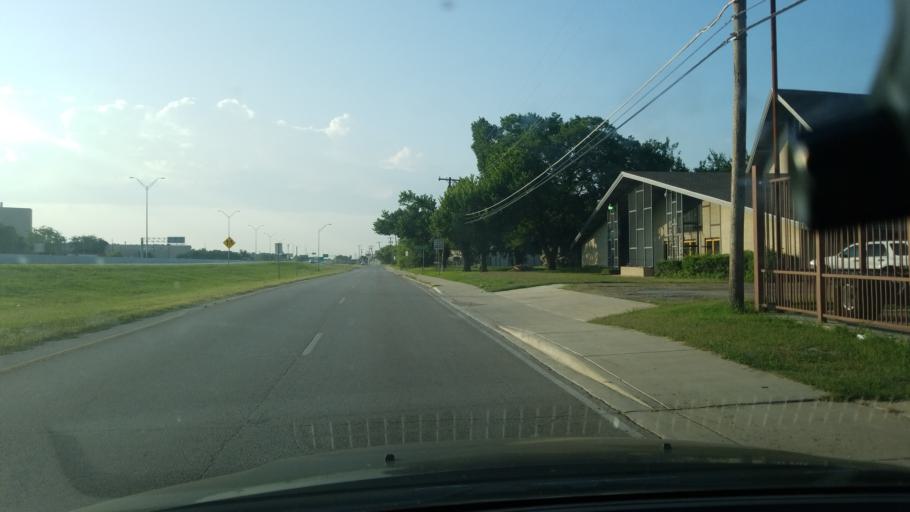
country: US
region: Texas
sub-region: Dallas County
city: Balch Springs
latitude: 32.7183
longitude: -96.6919
